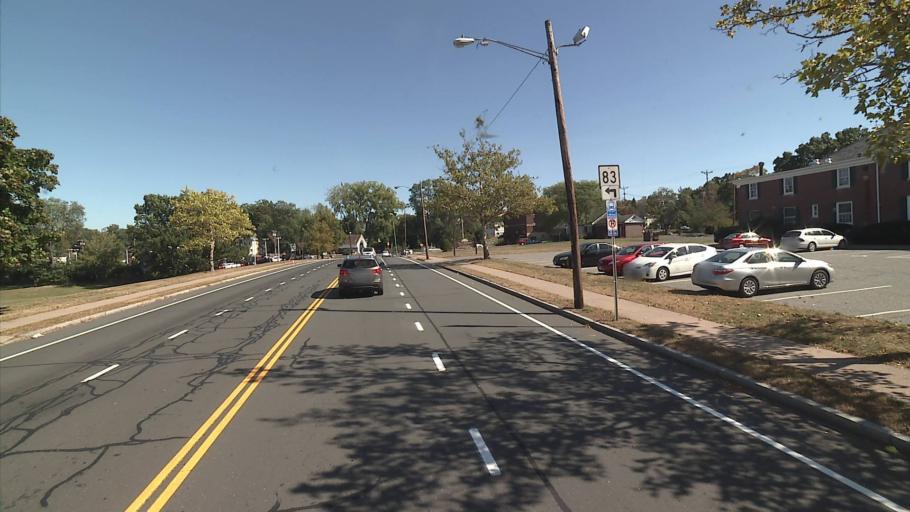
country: US
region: Connecticut
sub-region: Hartford County
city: Manchester
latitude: 41.7952
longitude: -72.5233
